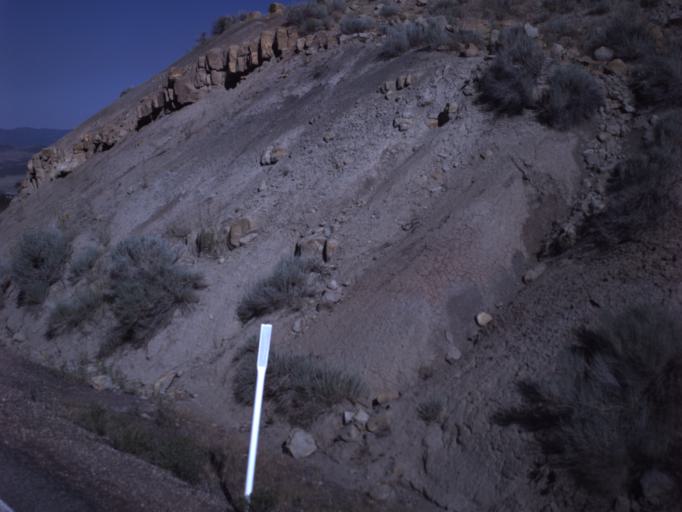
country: US
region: Utah
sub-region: Sanpete County
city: Fairview
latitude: 39.6480
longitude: -111.3775
